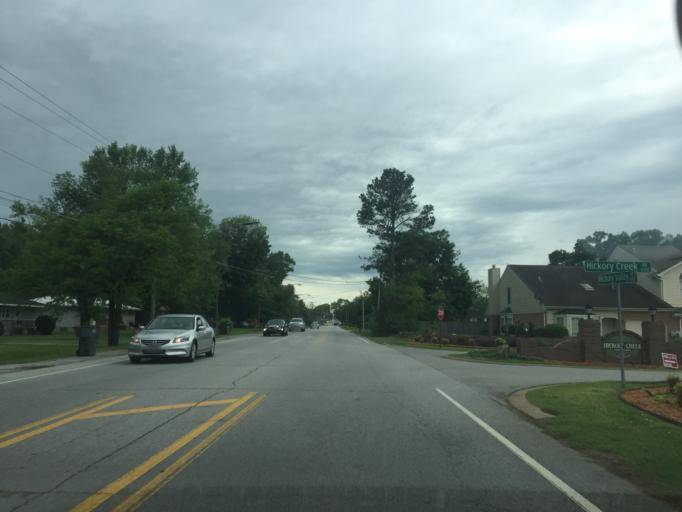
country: US
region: Tennessee
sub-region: Hamilton County
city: East Brainerd
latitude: 35.0511
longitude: -85.1637
